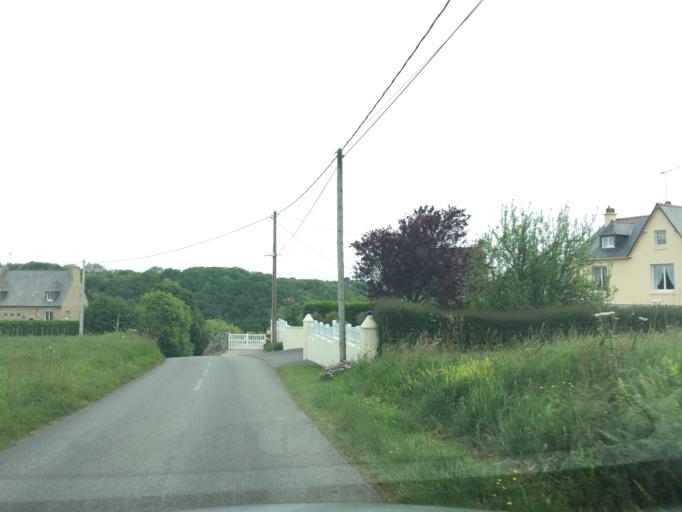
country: FR
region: Brittany
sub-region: Departement des Cotes-d'Armor
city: Crehen
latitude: 48.5925
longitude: -2.2224
